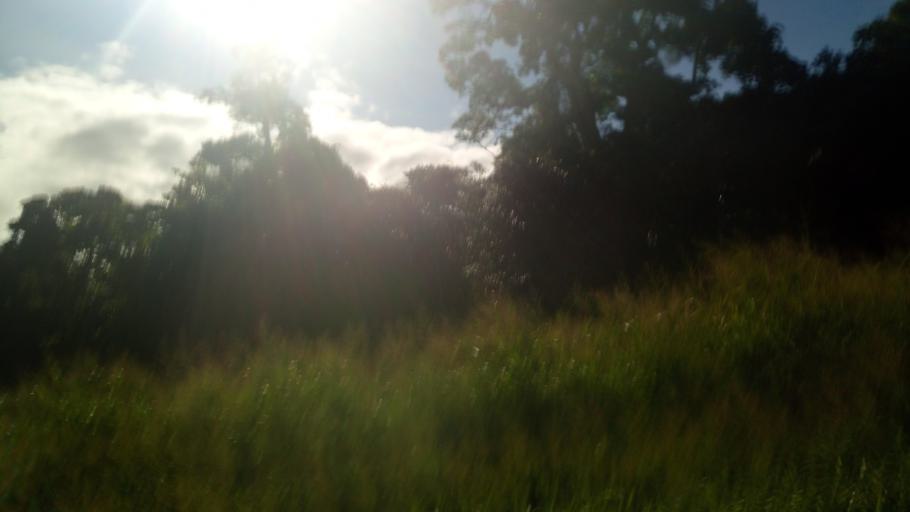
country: AU
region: Queensland
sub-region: Cassowary Coast
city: Innisfail
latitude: -17.5253
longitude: 145.9830
